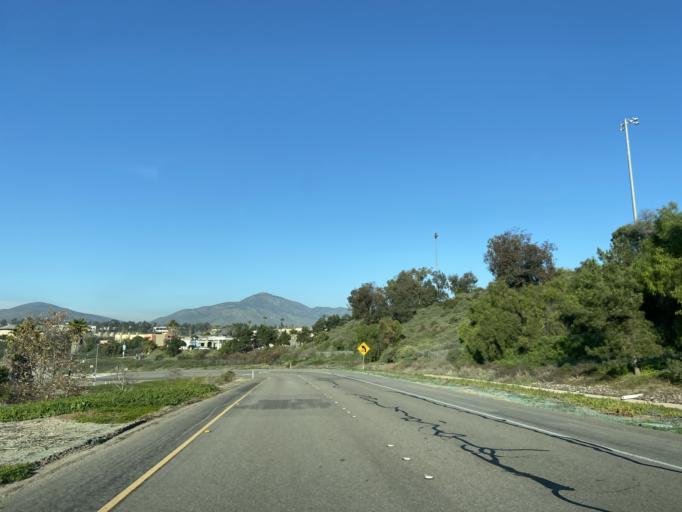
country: US
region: California
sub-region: San Diego County
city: Bonita
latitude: 32.6442
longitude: -116.9697
